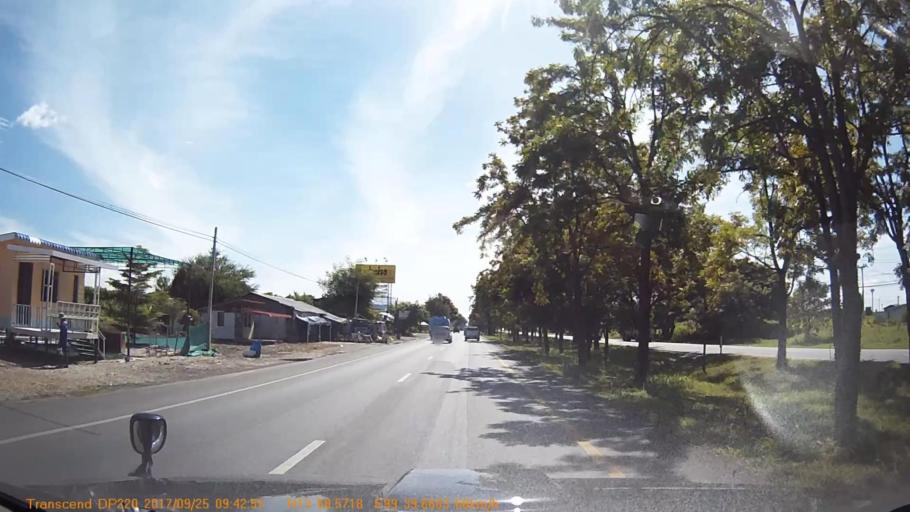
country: TH
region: Kanchanaburi
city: Tha Muang
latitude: 13.9761
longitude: 99.6614
